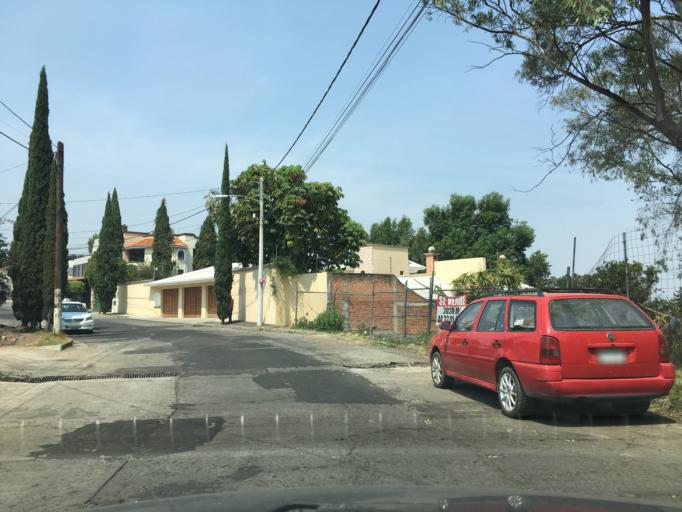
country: MX
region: Michoacan
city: Morelia
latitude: 19.6777
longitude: -101.1873
